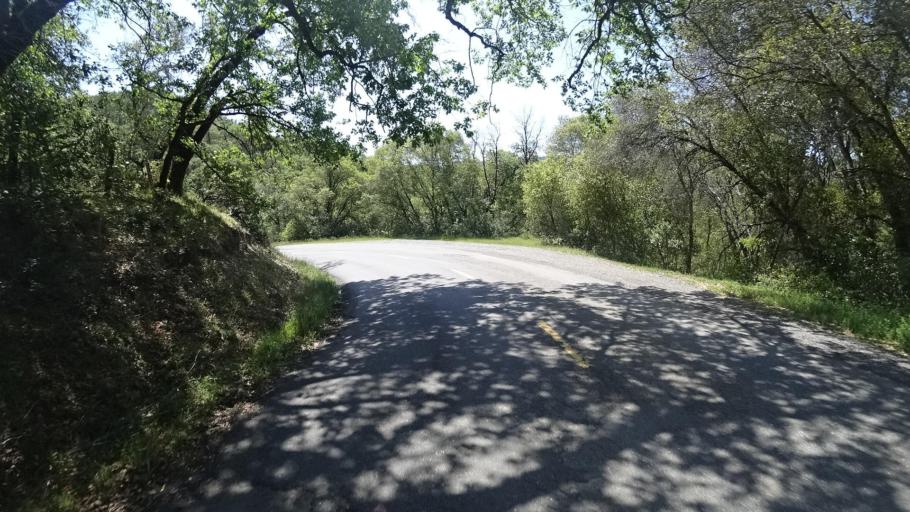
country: US
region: California
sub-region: Humboldt County
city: Redway
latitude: 40.1759
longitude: -123.6002
